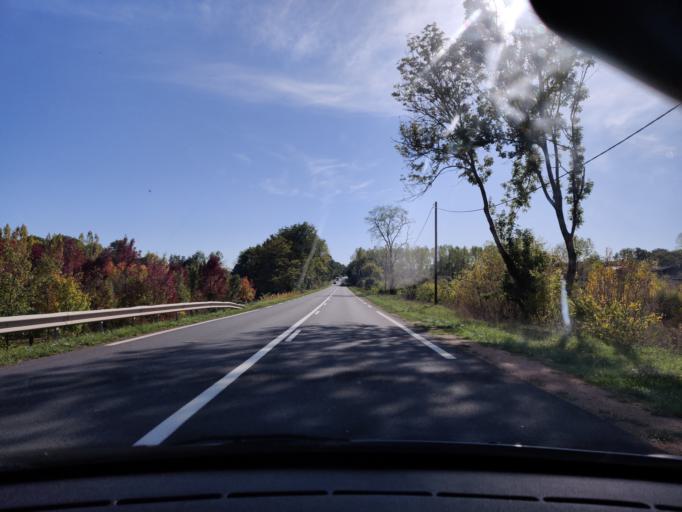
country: FR
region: Auvergne
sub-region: Departement du Puy-de-Dome
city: Combronde
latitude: 46.0099
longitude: 3.0913
